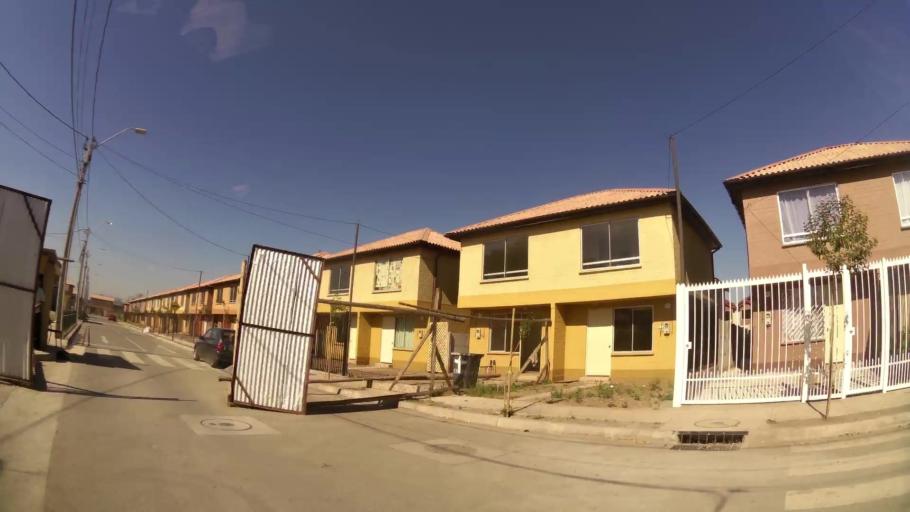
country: CL
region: Santiago Metropolitan
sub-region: Provincia de Maipo
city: San Bernardo
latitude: -33.6114
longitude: -70.6788
